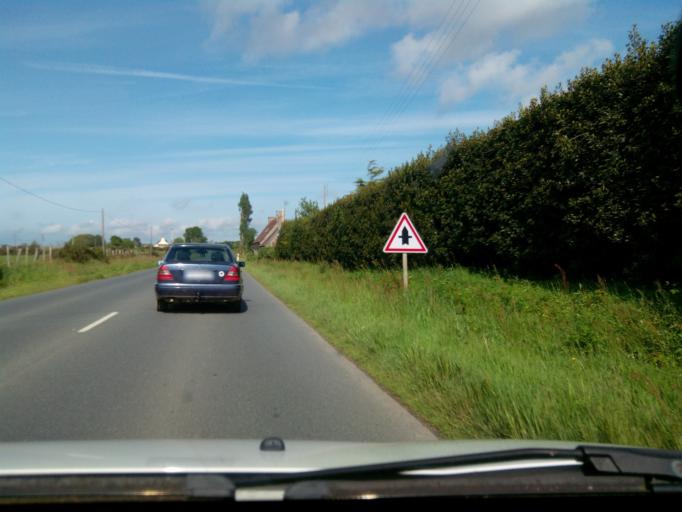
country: FR
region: Brittany
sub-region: Departement des Cotes-d'Armor
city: Louannec
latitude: 48.7780
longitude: -3.4123
